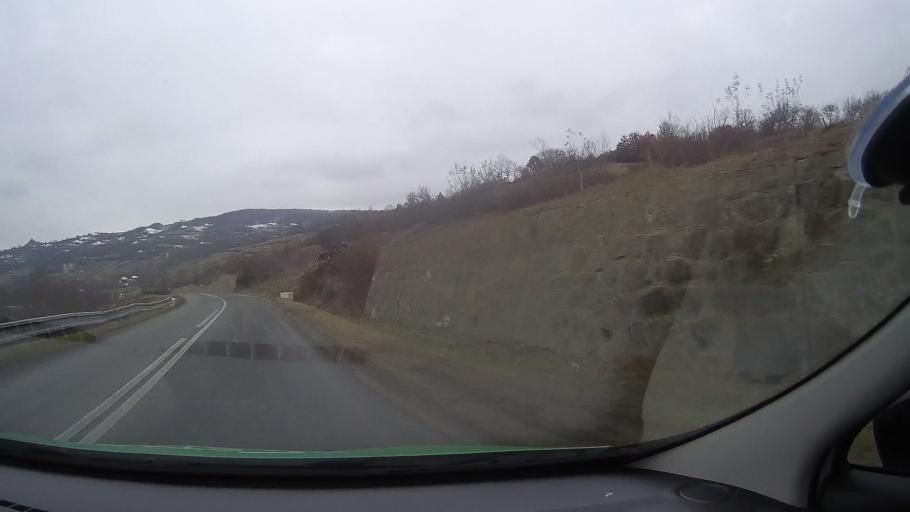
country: RO
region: Alba
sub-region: Comuna Metes
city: Metes
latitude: 46.1070
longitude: 23.4415
